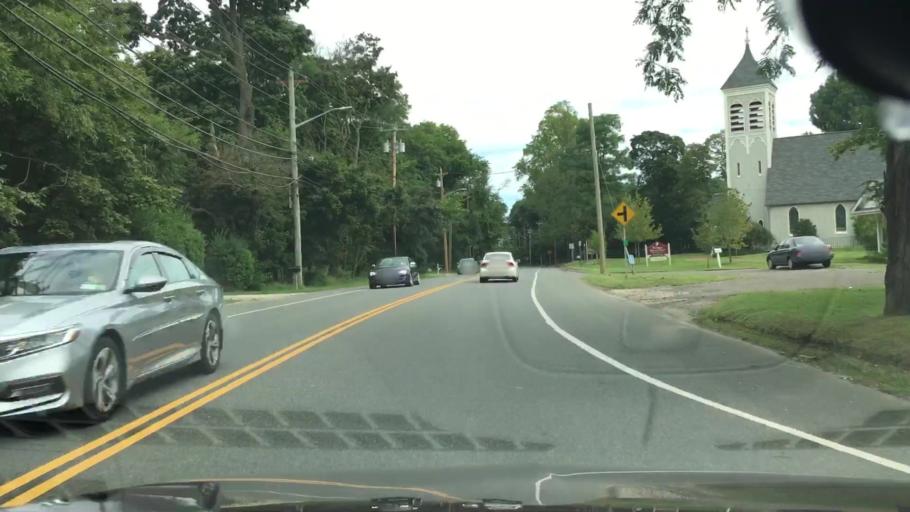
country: US
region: New York
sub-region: Suffolk County
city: Saint James
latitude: 40.8838
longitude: -73.1649
